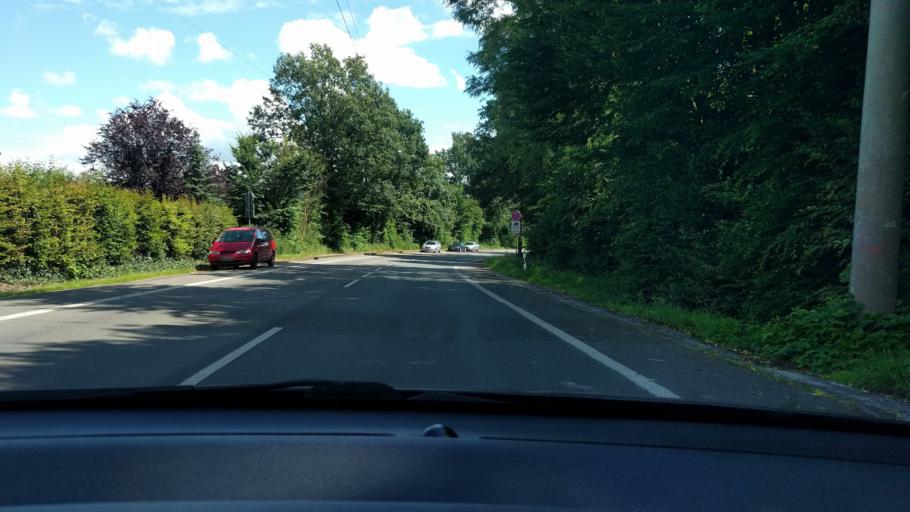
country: DE
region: North Rhine-Westphalia
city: Datteln
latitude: 51.6592
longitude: 7.3359
